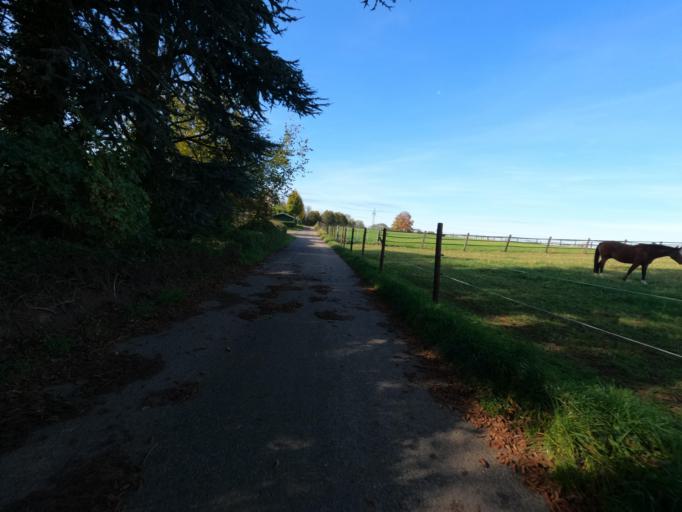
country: DE
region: North Rhine-Westphalia
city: Erkelenz
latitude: 51.0357
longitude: 6.3155
